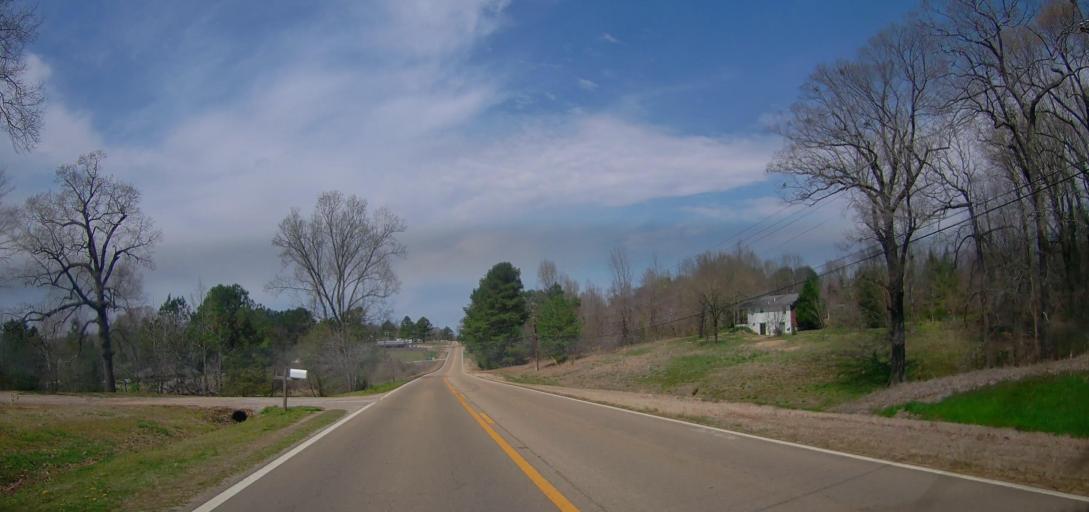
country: US
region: Mississippi
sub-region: Union County
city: New Albany
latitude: 34.4493
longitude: -88.9696
